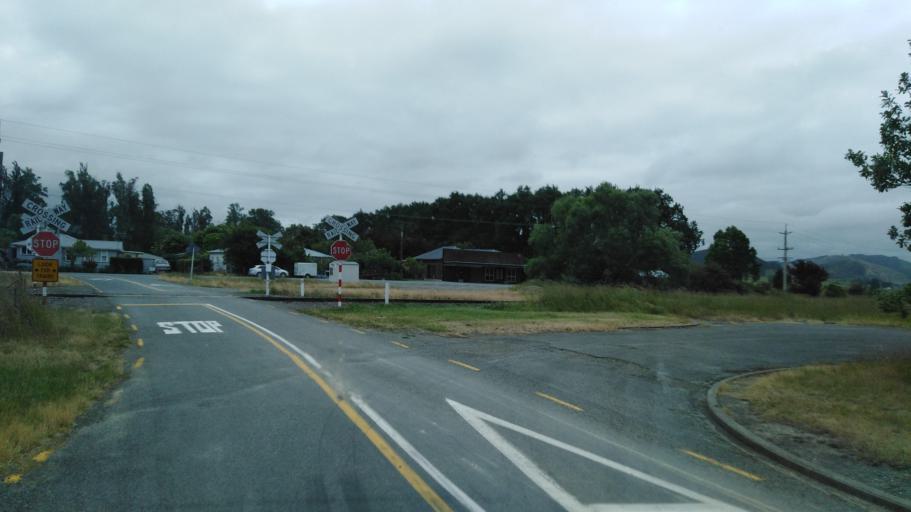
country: NZ
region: Canterbury
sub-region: Kaikoura District
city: Kaikoura
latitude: -42.7103
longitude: 173.2925
